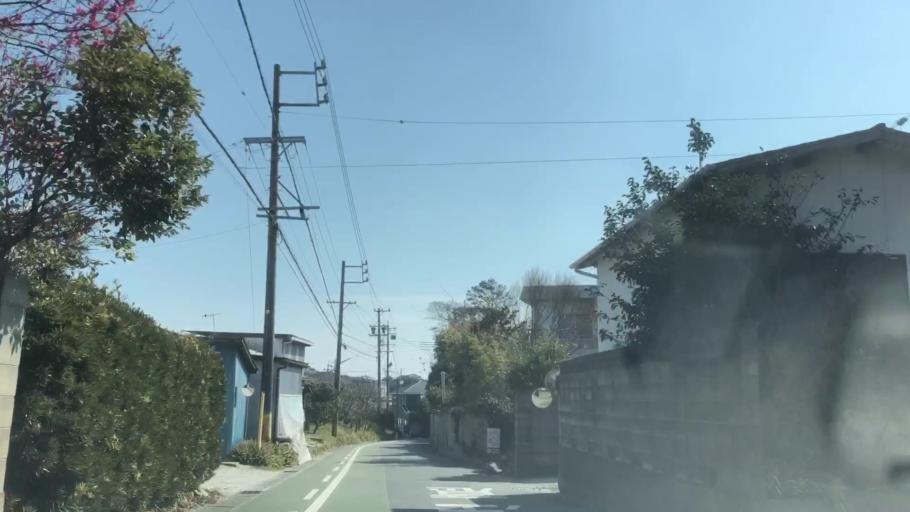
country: JP
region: Aichi
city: Tahara
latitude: 34.6661
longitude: 137.2569
